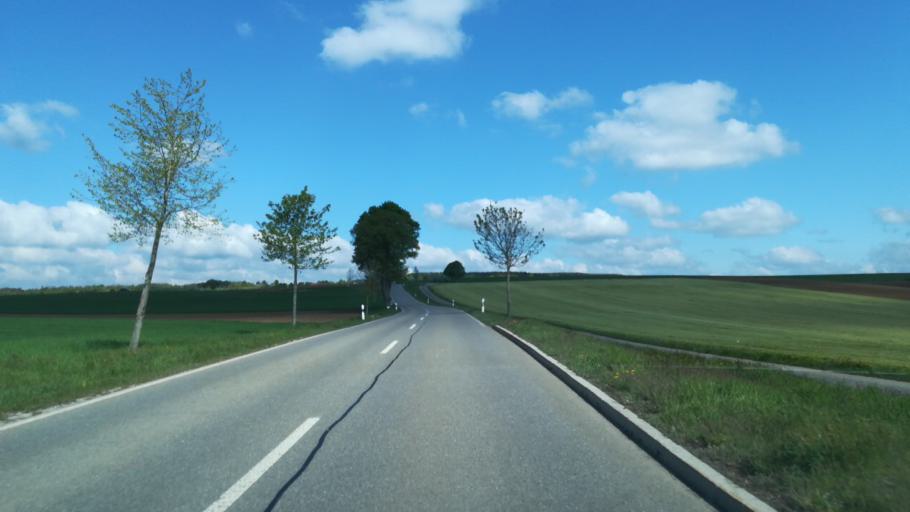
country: DE
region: Baden-Wuerttemberg
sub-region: Freiburg Region
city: Eggingen
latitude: 47.7595
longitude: 8.3825
